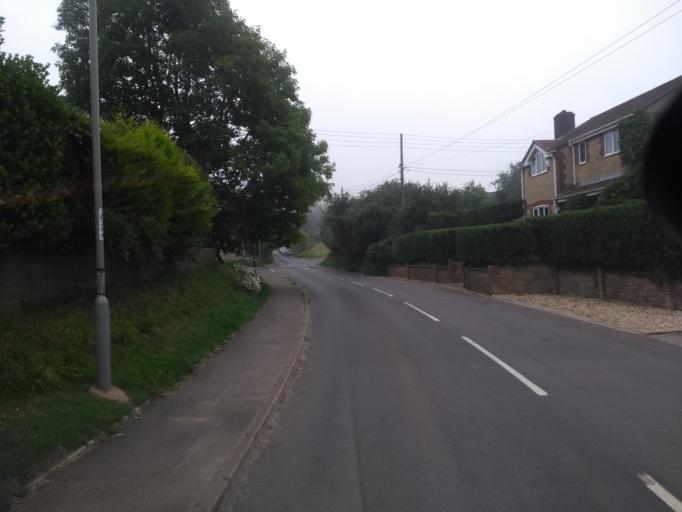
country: GB
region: England
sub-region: Dorset
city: Beaminster
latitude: 50.8184
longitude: -2.7984
